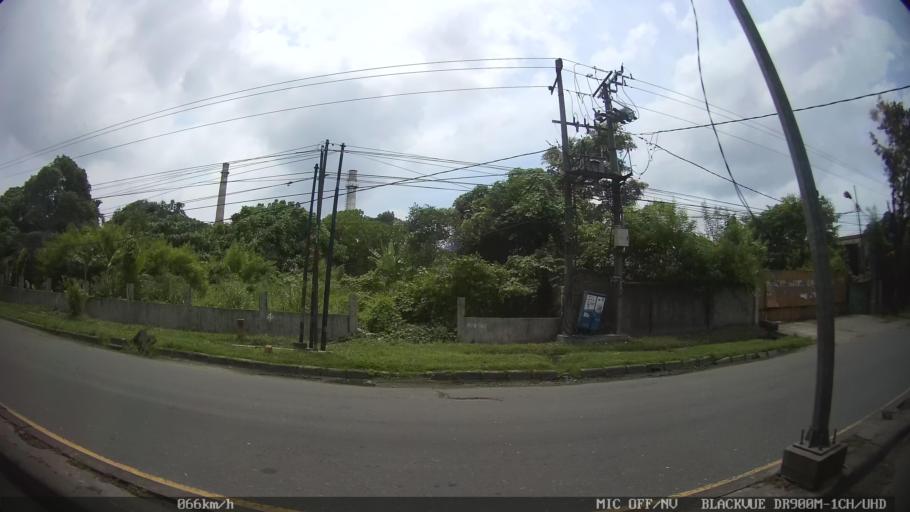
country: ID
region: North Sumatra
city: Labuhan Deli
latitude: 3.6702
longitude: 98.6671
